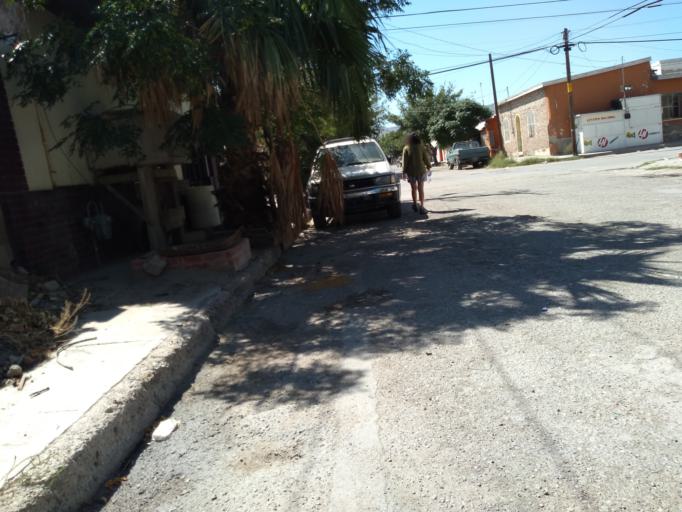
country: US
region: Texas
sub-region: El Paso County
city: El Paso
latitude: 31.7472
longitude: -106.4933
